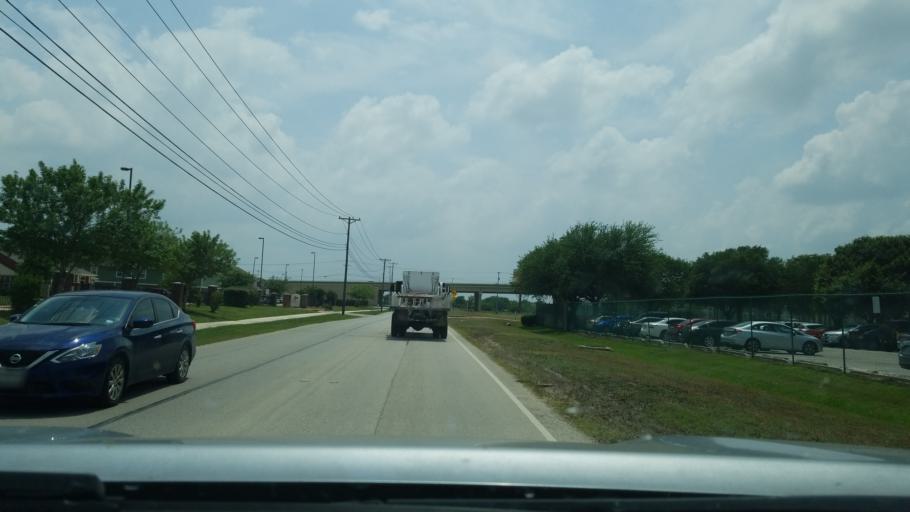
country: US
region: Texas
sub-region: Comal County
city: New Braunfels
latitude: 29.7387
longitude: -98.0858
